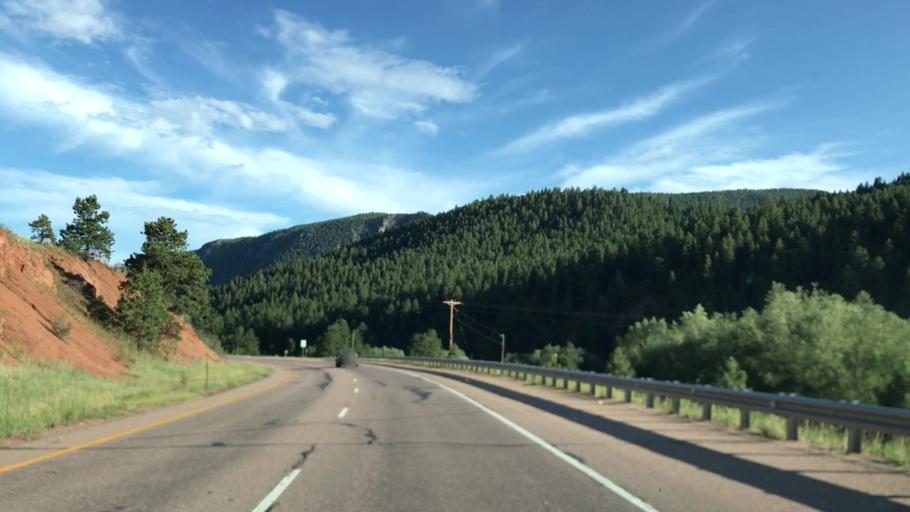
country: US
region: Colorado
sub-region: El Paso County
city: Cascade-Chipita Park
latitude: 38.9509
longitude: -105.0259
